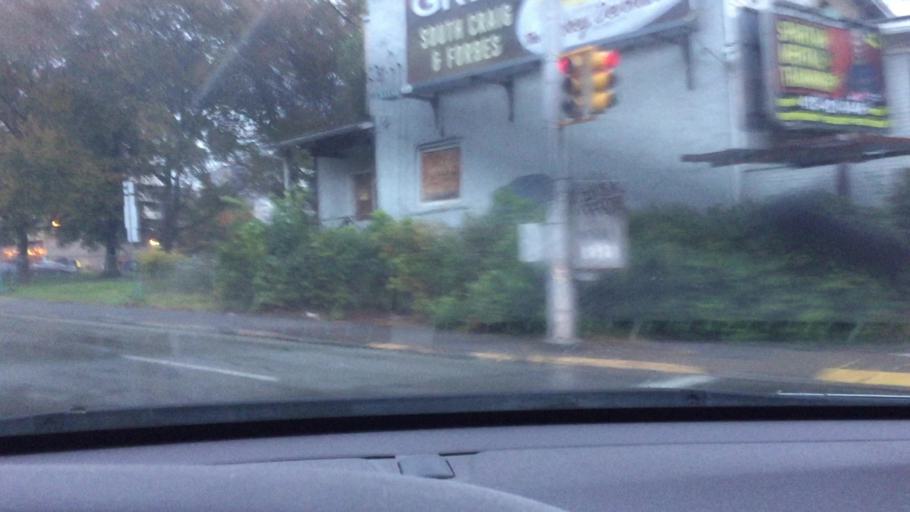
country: US
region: Pennsylvania
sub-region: Allegheny County
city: Bloomfield
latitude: 40.4353
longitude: -79.9564
